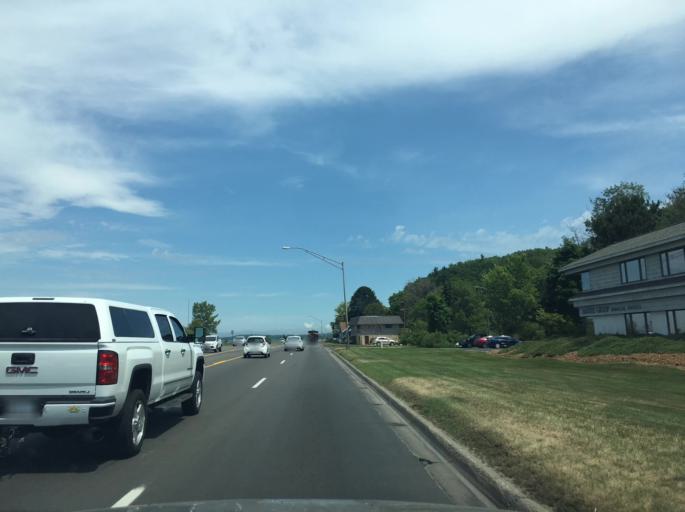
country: US
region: Michigan
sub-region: Grand Traverse County
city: Traverse City
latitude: 44.7507
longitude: -85.5233
